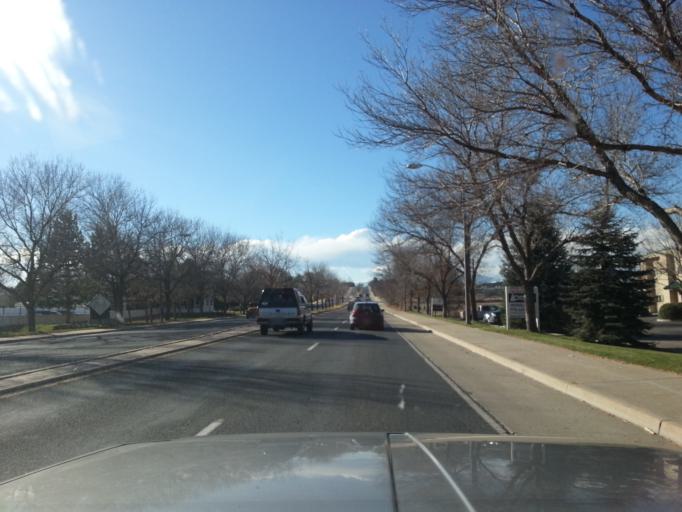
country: US
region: Colorado
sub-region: Larimer County
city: Loveland
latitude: 40.3784
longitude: -105.0786
